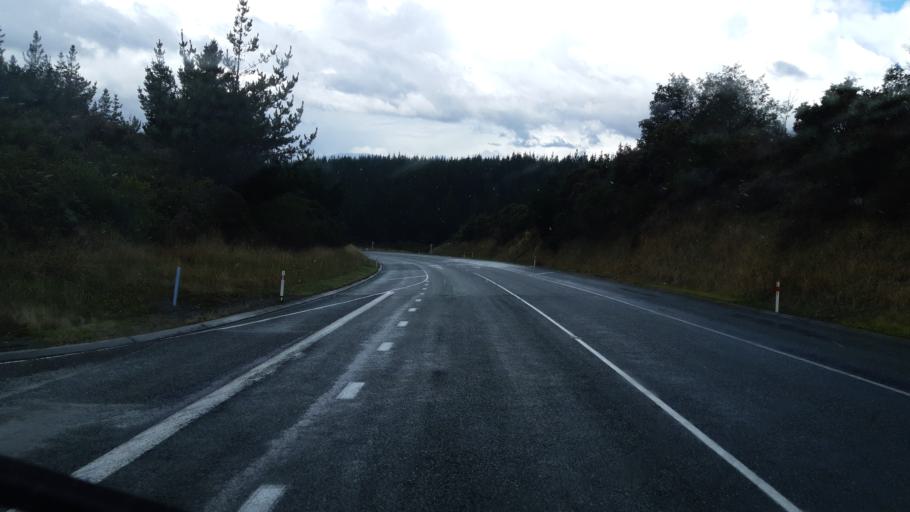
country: NZ
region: Tasman
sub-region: Tasman District
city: Wakefield
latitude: -41.4788
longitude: 172.9243
